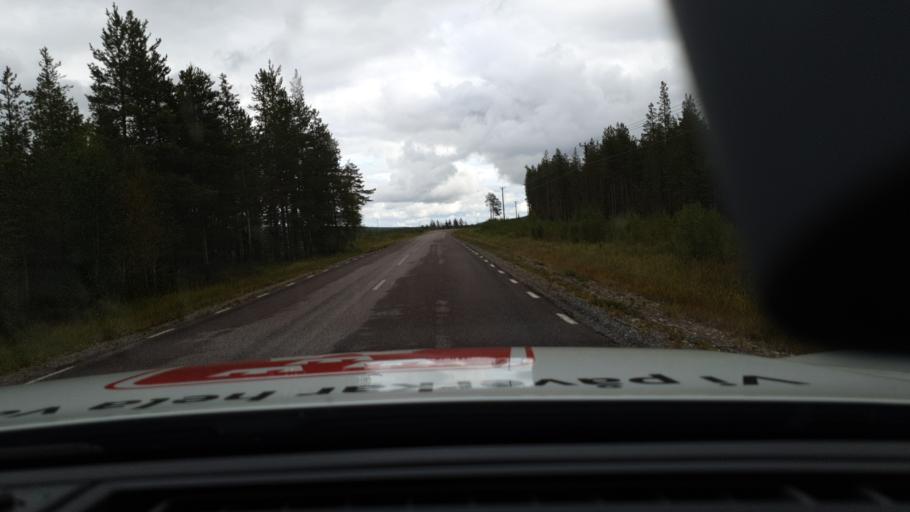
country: SE
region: Norrbotten
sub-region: Gallivare Kommun
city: Gaellivare
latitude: 66.9162
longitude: 21.6435
